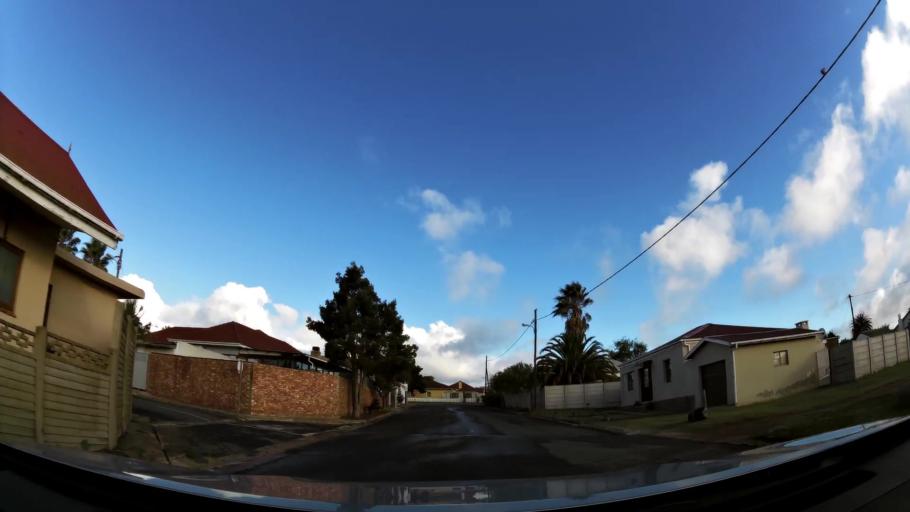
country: ZA
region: Western Cape
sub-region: Eden District Municipality
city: Riversdale
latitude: -34.2047
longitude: 21.5860
